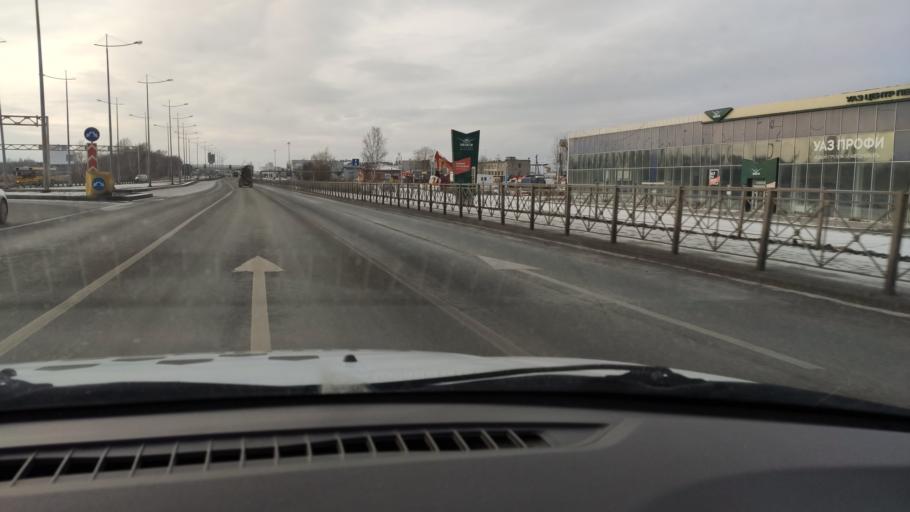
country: RU
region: Perm
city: Kondratovo
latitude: 57.9478
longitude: 56.0899
